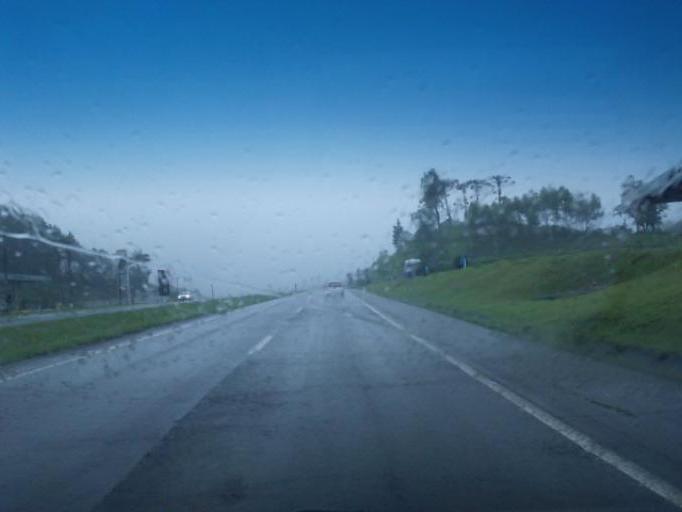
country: BR
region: Parana
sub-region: Antonina
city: Antonina
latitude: -25.1095
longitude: -48.7468
